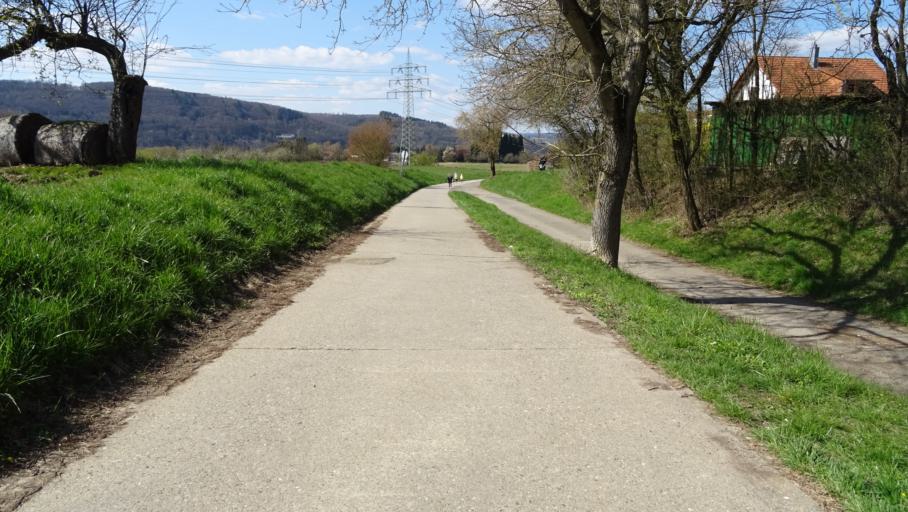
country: DE
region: Baden-Wuerttemberg
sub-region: Karlsruhe Region
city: Neckarzimmern
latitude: 49.3320
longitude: 9.1188
